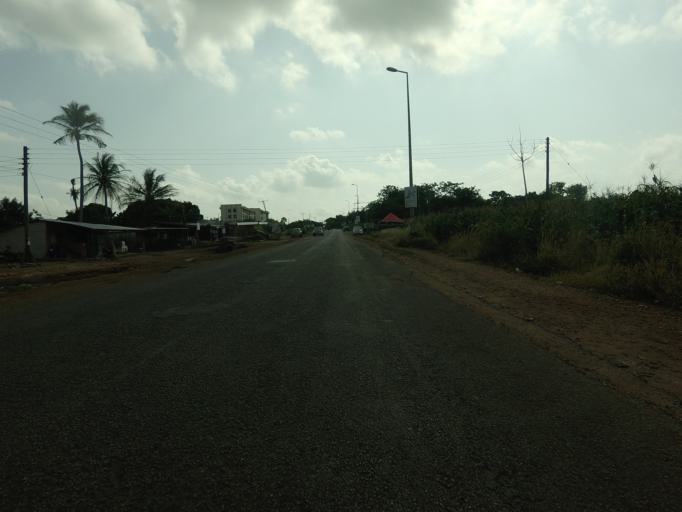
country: GH
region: Volta
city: Ho
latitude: 6.6005
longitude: 0.5024
